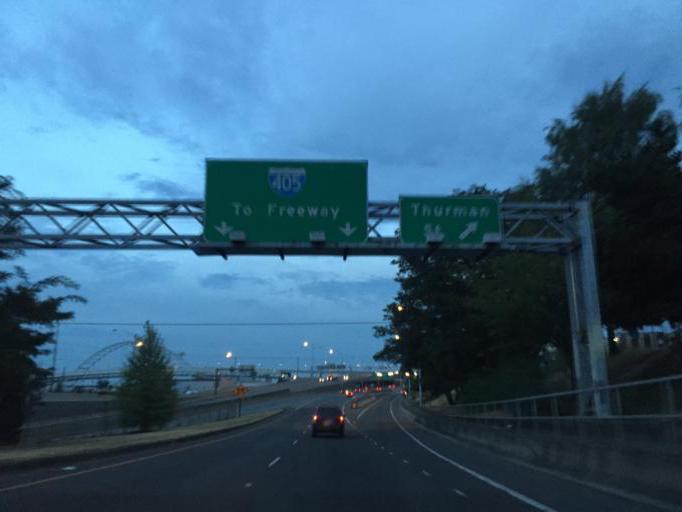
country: US
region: Oregon
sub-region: Multnomah County
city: Portland
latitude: 45.5367
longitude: -122.6974
